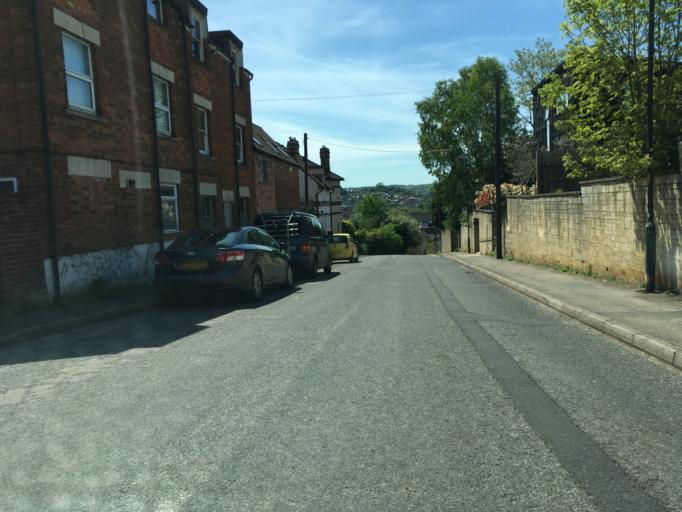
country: GB
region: England
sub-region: Gloucestershire
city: Stroud
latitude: 51.7498
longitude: -2.2132
